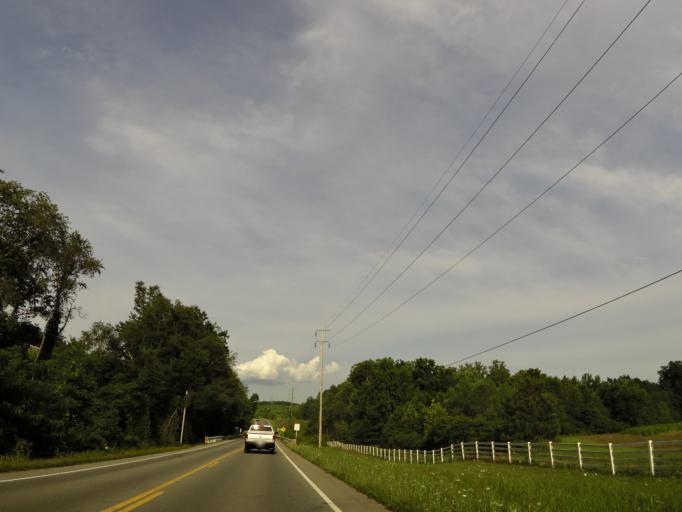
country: US
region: Tennessee
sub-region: Humphreys County
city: McEwen
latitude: 36.0931
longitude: -87.5559
